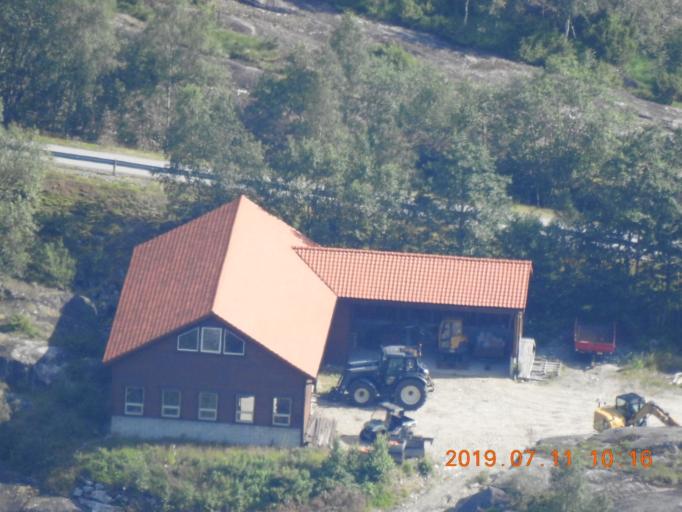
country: NO
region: Vest-Agder
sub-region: Sirdal
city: Tonstad
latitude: 59.0444
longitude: 6.6445
